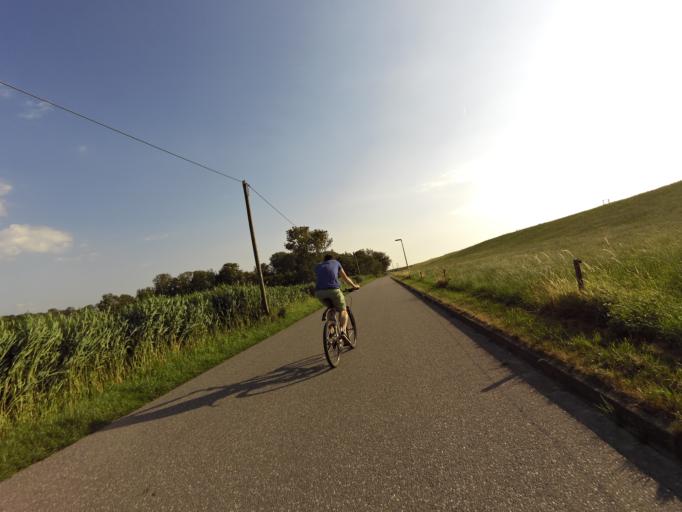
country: DE
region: Lower Saxony
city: Nordholz
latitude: 53.7995
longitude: 8.5659
